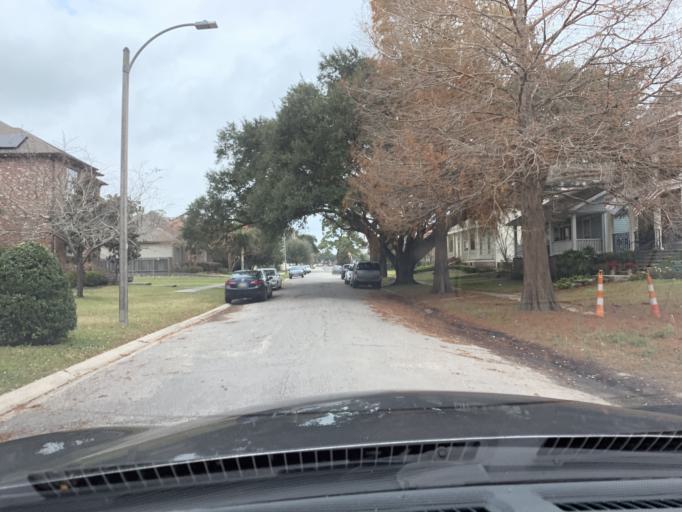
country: US
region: Louisiana
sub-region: Jefferson Parish
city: Metairie
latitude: 30.0159
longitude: -90.1024
